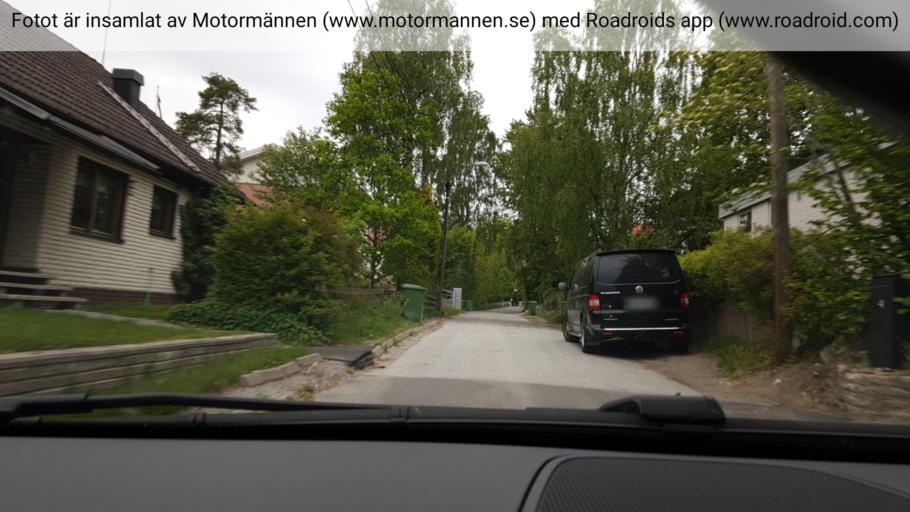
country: SE
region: Stockholm
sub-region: Huddinge Kommun
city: Huddinge
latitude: 59.2245
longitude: 18.0041
